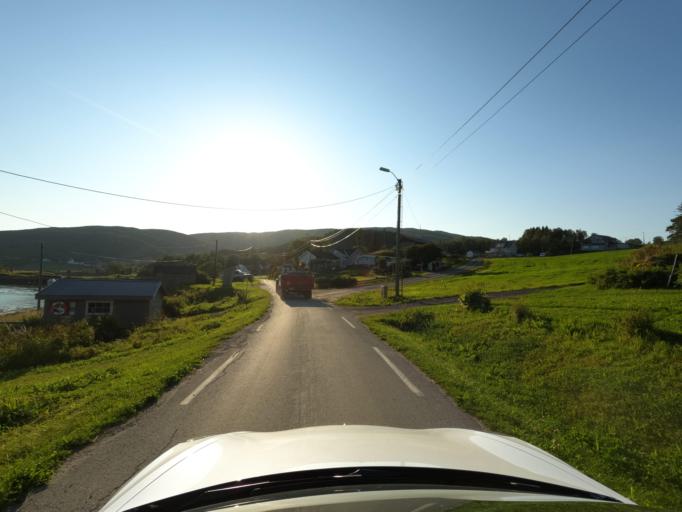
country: NO
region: Troms
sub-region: Skanland
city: Evenskjer
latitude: 68.4557
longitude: 16.6036
